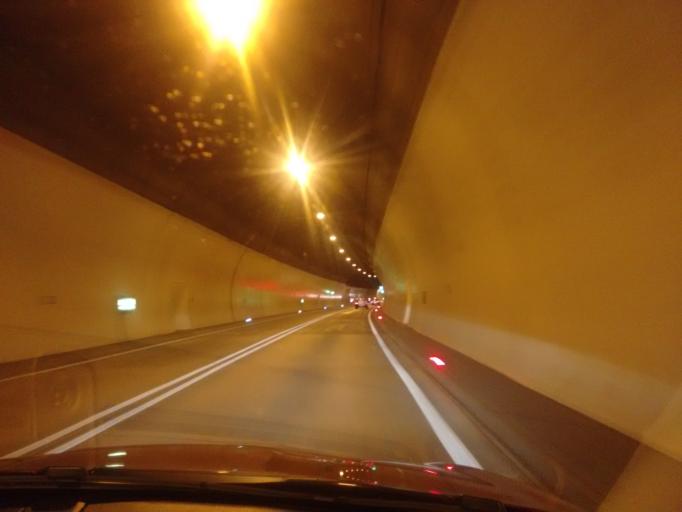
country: AT
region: Upper Austria
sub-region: Politischer Bezirk Gmunden
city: Ebensee
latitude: 47.8465
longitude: 13.7799
